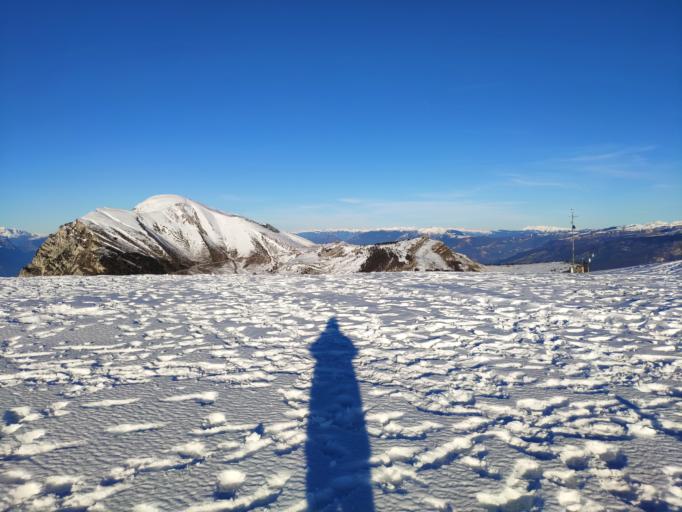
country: IT
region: Veneto
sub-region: Provincia di Verona
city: Malcesine
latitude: 45.7728
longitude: 10.8647
